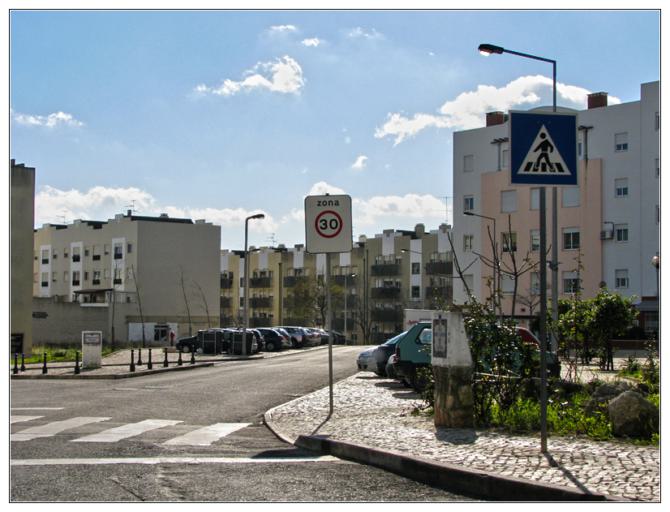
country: PT
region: Lisbon
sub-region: Cascais
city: Sao Domingos de Rana
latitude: 38.7005
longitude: -9.3395
